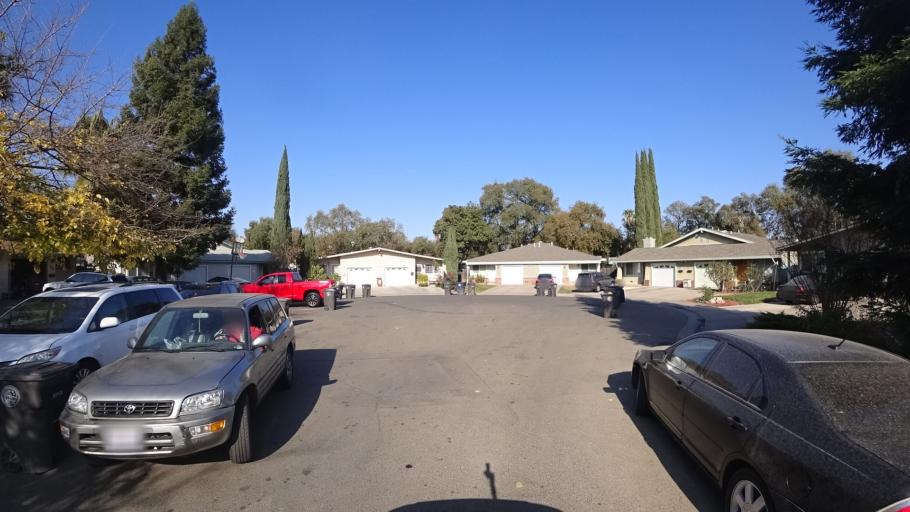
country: US
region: California
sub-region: Sacramento County
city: Citrus Heights
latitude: 38.6818
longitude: -121.2837
